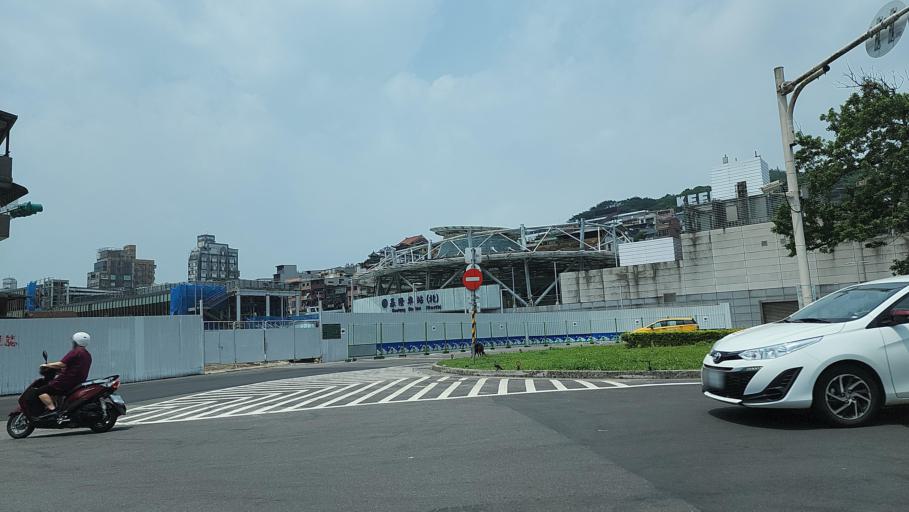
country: TW
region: Taiwan
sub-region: Keelung
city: Keelung
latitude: 25.1336
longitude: 121.7414
